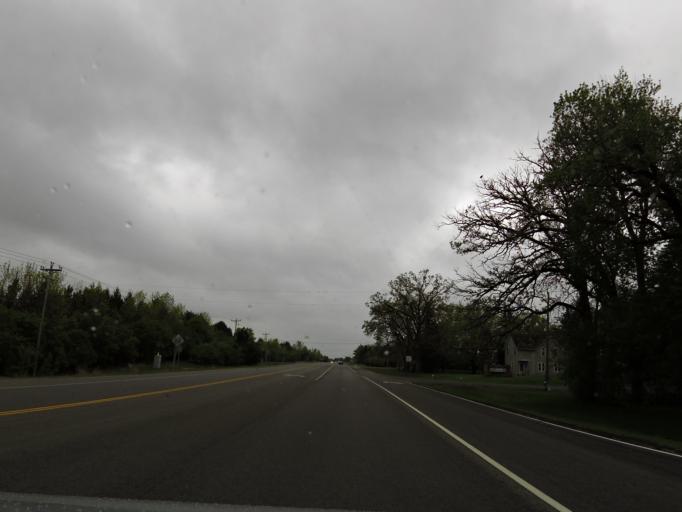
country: US
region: Minnesota
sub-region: Washington County
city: Lake Elmo
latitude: 45.0256
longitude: -92.8567
